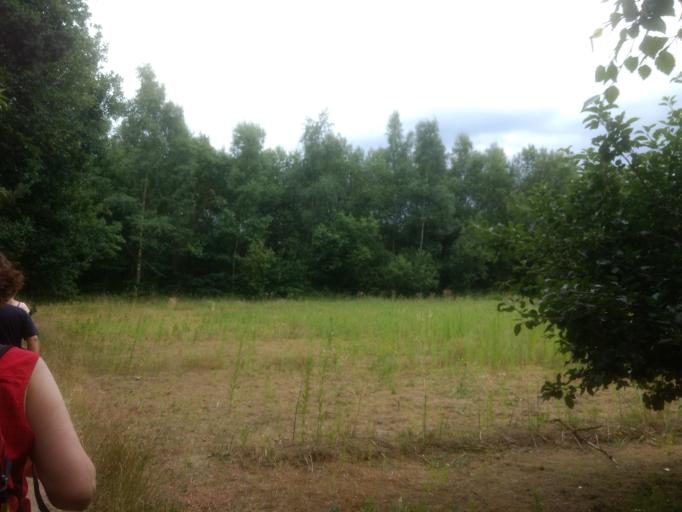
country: BE
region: Flanders
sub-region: Provincie Vlaams-Brabant
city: Tremelo
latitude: 50.9854
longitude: 4.6909
